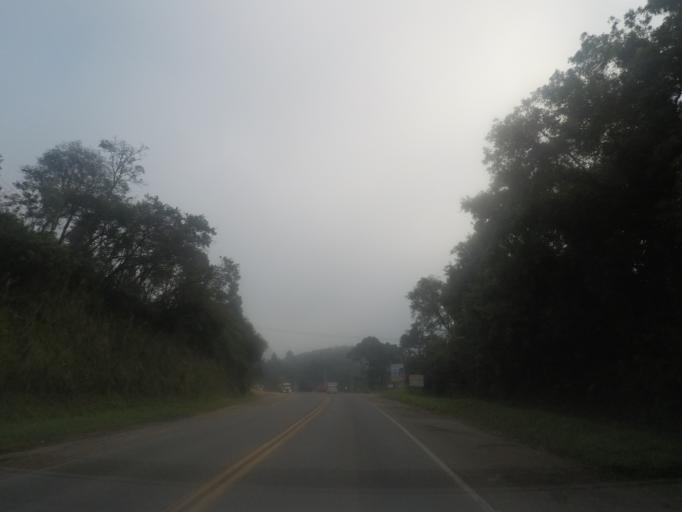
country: BR
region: Parana
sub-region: Almirante Tamandare
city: Almirante Tamandare
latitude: -25.2904
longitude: -49.3053
